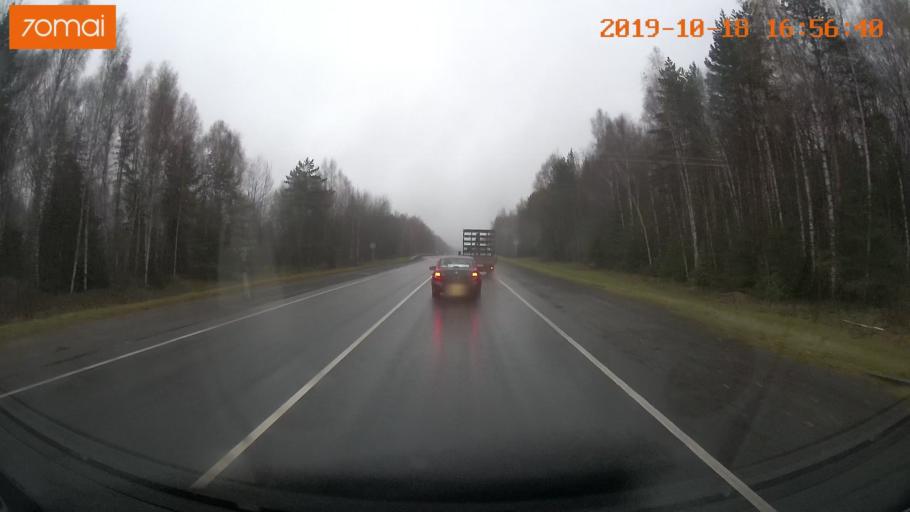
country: RU
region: Ivanovo
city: Novoye Leushino
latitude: 56.6591
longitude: 40.5896
